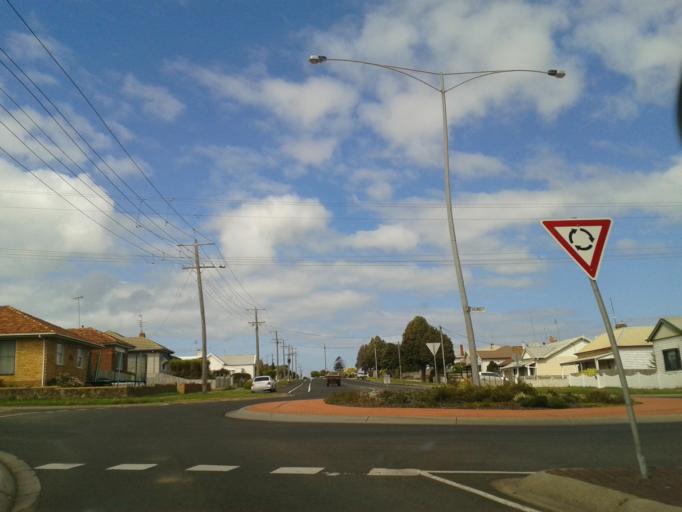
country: AU
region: Victoria
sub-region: Glenelg
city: Portland
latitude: -38.3420
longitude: 141.6010
